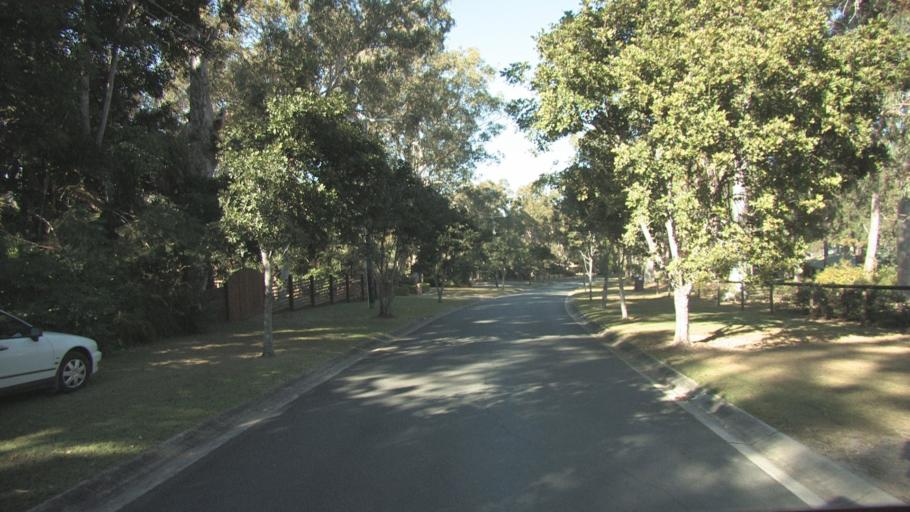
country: AU
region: Queensland
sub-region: Brisbane
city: Forest Lake
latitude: -27.6704
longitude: 153.0101
